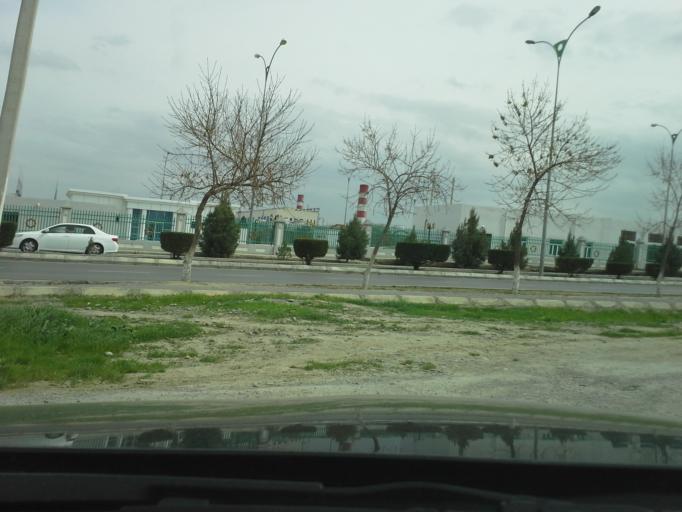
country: TM
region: Ahal
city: Abadan
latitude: 38.0622
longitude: 58.1591
